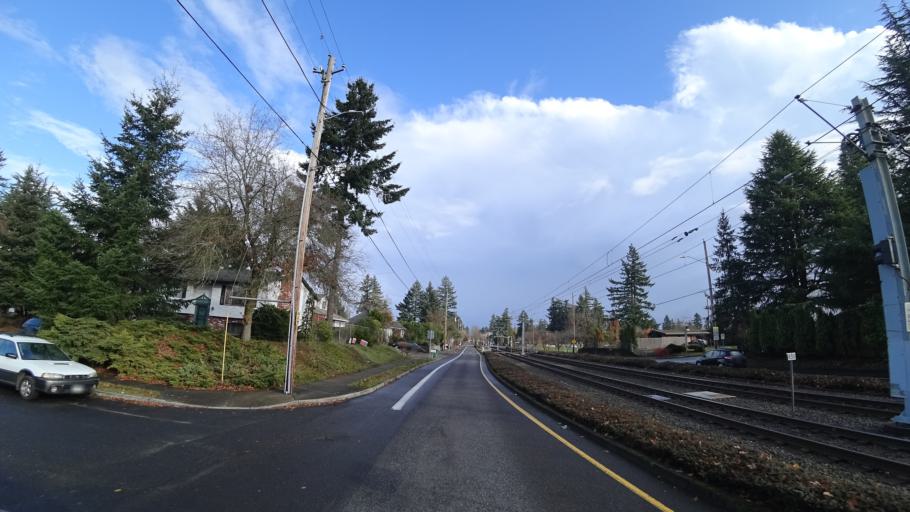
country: US
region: Oregon
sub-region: Multnomah County
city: Lents
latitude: 45.5227
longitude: -122.5459
